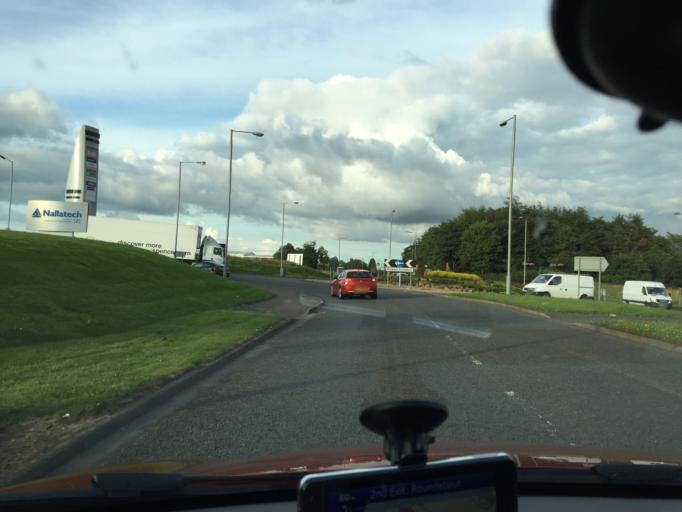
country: GB
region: Scotland
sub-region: North Lanarkshire
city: Cumbernauld
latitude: 55.9702
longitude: -3.9641
